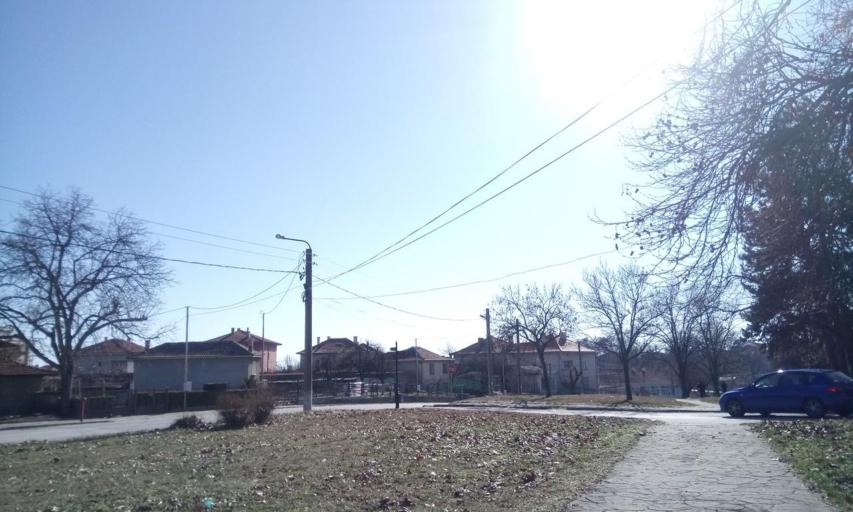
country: BG
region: Plovdiv
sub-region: Obshtina Khisarya
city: Khisarya
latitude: 42.5100
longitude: 24.7146
